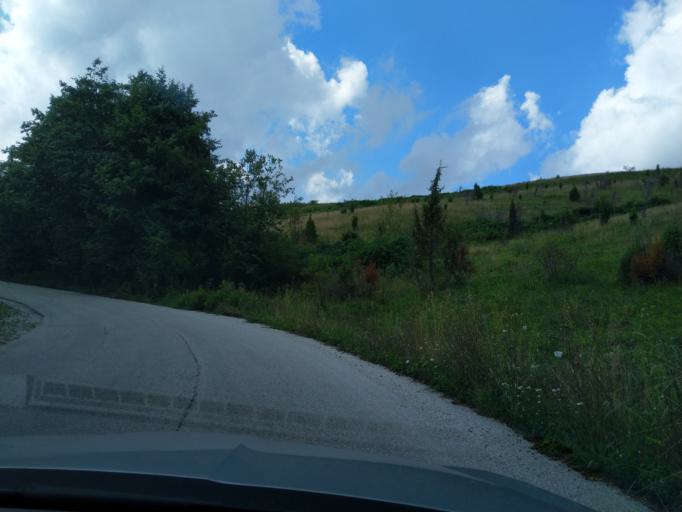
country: RS
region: Central Serbia
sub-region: Zlatiborski Okrug
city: Nova Varos
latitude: 43.5576
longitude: 19.9030
